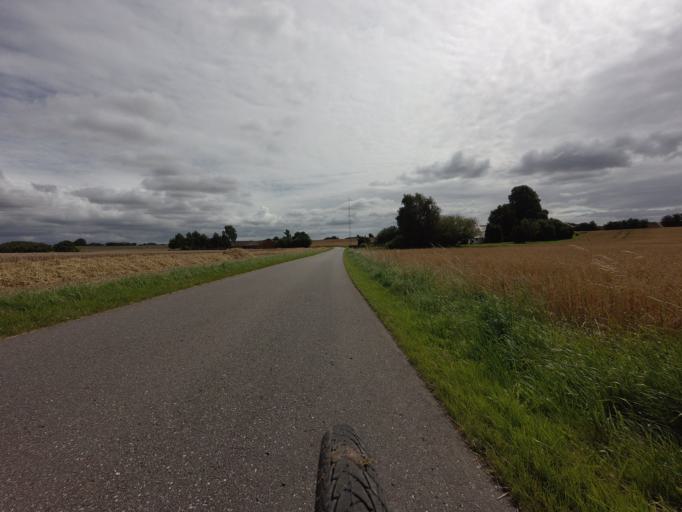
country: DK
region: Central Jutland
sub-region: Syddjurs Kommune
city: Ryomgard
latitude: 56.4036
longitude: 10.5410
